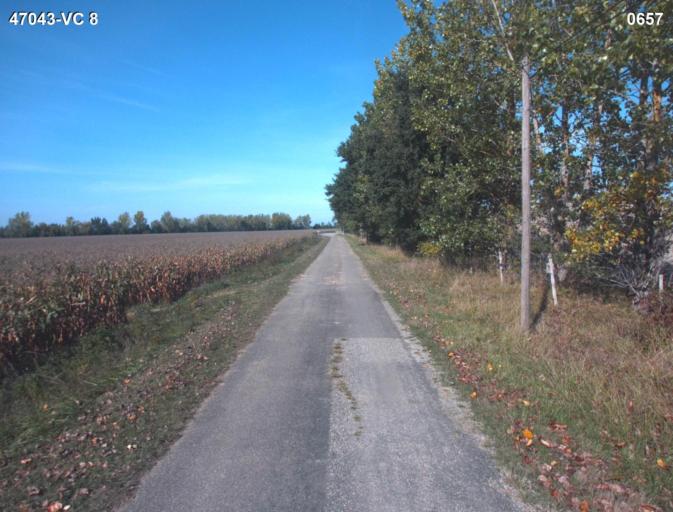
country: FR
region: Aquitaine
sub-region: Departement du Lot-et-Garonne
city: Buzet-sur-Baise
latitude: 44.2750
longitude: 0.2909
